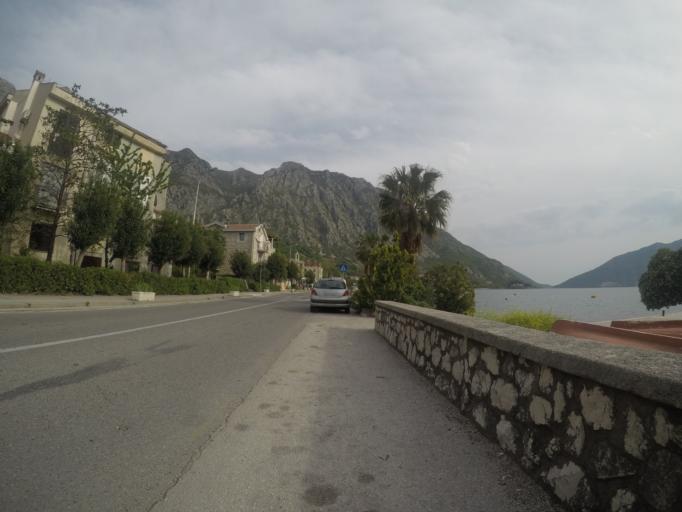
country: ME
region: Kotor
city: Risan
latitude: 42.5121
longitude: 18.6920
